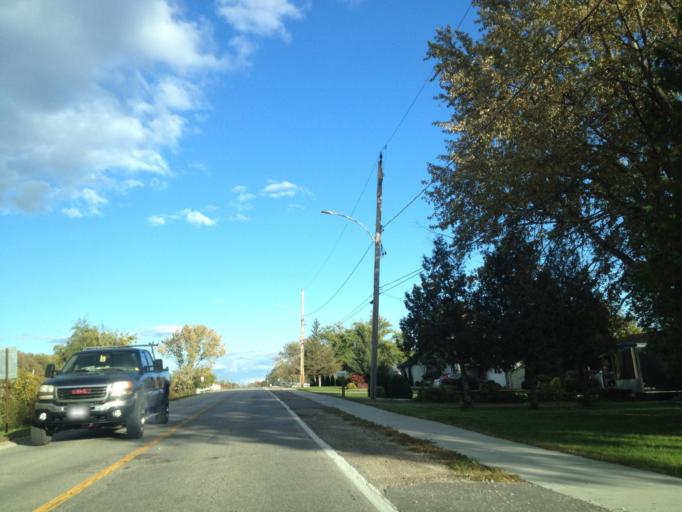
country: US
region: Michigan
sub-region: Wayne County
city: Grosse Pointe Farms
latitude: 42.2966
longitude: -82.6904
